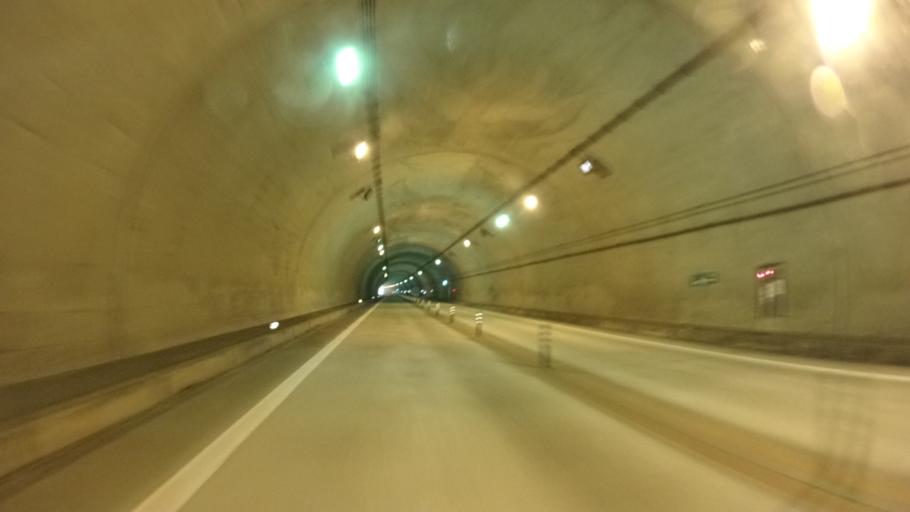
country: JP
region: Toyama
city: Himi
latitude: 36.8927
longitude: 136.9830
